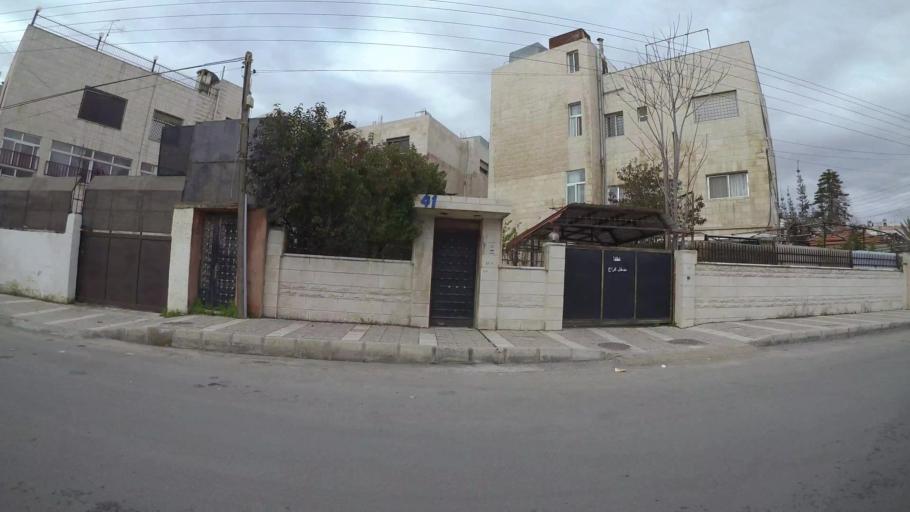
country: JO
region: Amman
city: Wadi as Sir
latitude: 31.9506
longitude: 35.8351
